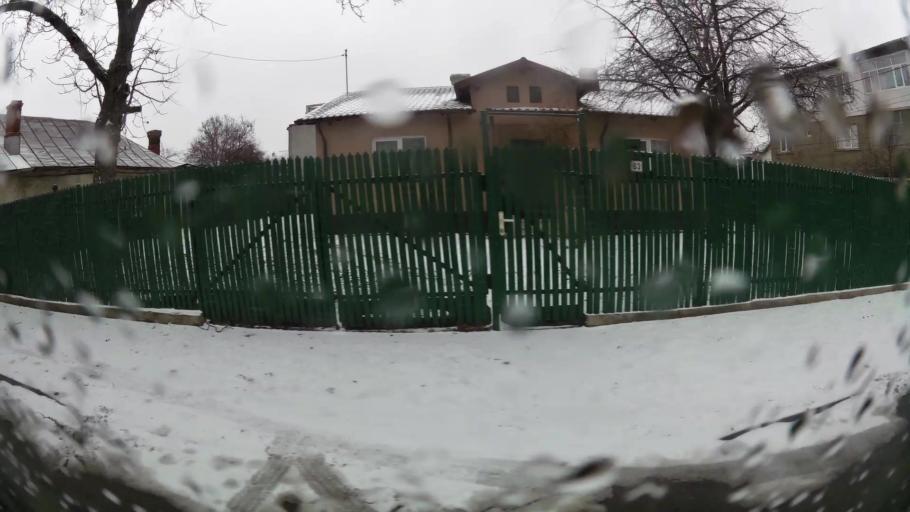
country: RO
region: Prahova
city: Ploiesti
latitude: 44.9445
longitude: 26.0098
